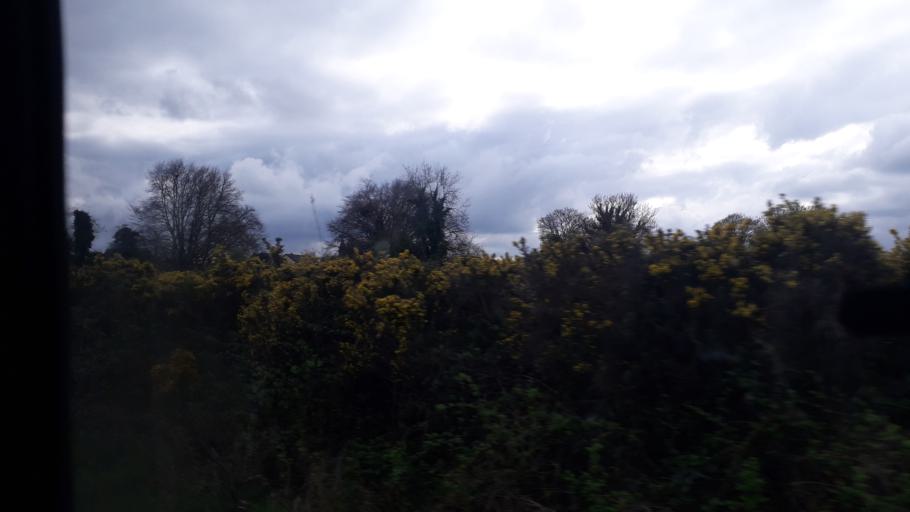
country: IE
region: Leinster
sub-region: An Longfort
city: Longford
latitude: 53.7717
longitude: -7.8317
